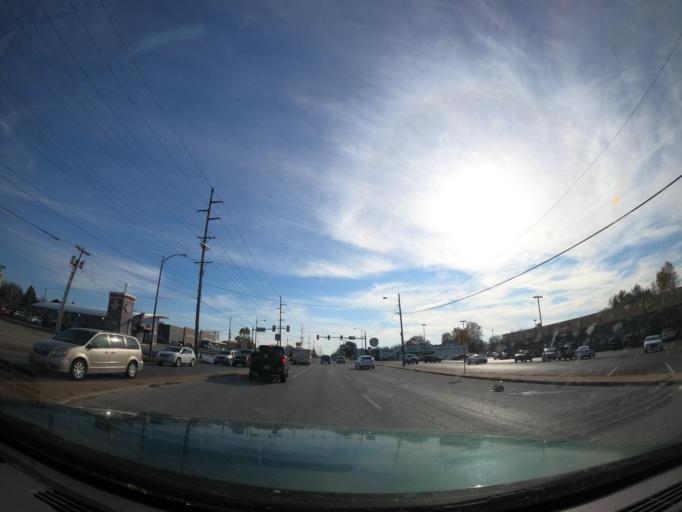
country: US
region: Oklahoma
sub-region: Tulsa County
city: Tulsa
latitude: 36.1251
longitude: -95.9403
